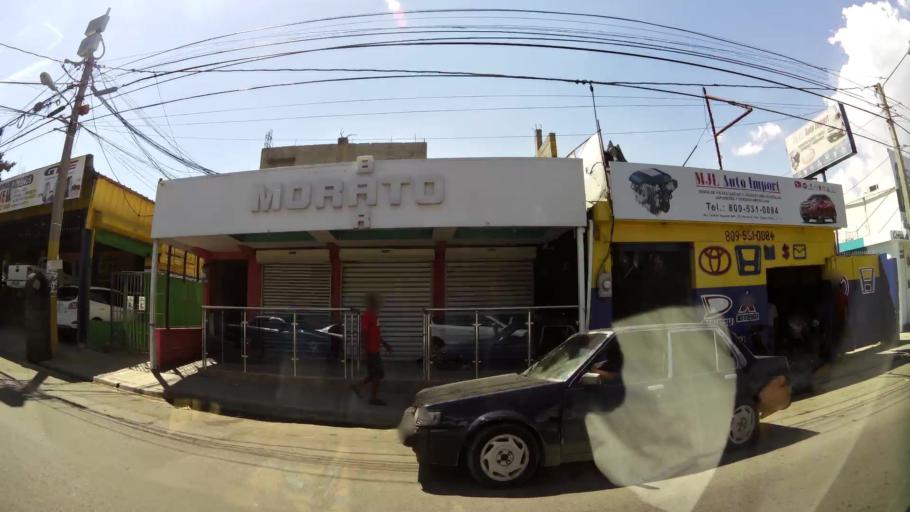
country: DO
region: Nacional
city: Bella Vista
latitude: 18.4548
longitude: -69.9779
